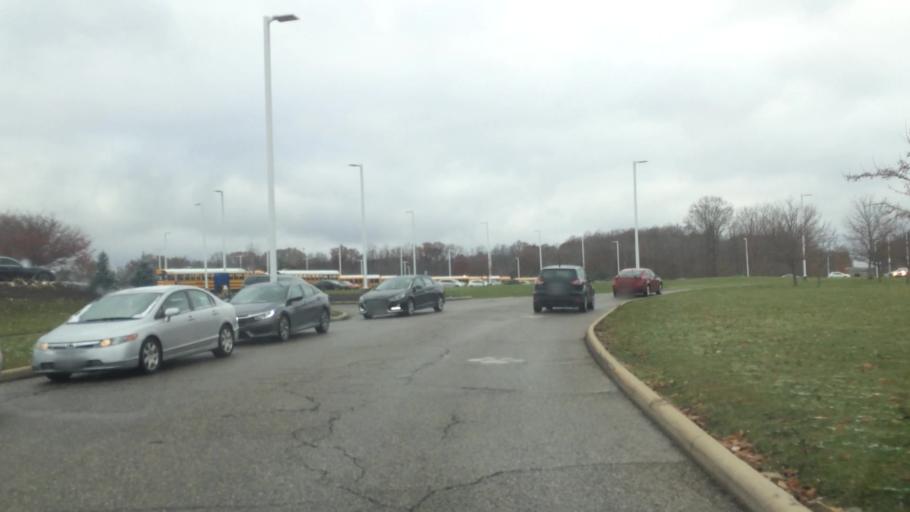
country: US
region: Ohio
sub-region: Summit County
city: Twinsburg
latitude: 41.3190
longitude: -81.4503
